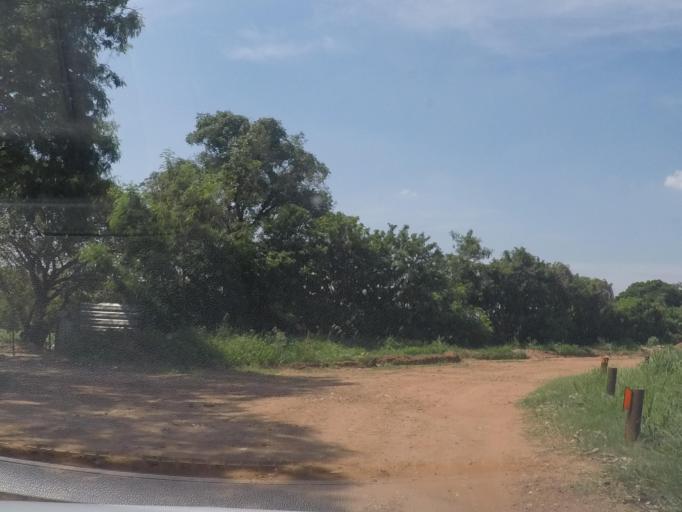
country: BR
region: Sao Paulo
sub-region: Sumare
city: Sumare
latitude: -22.8804
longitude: -47.2977
